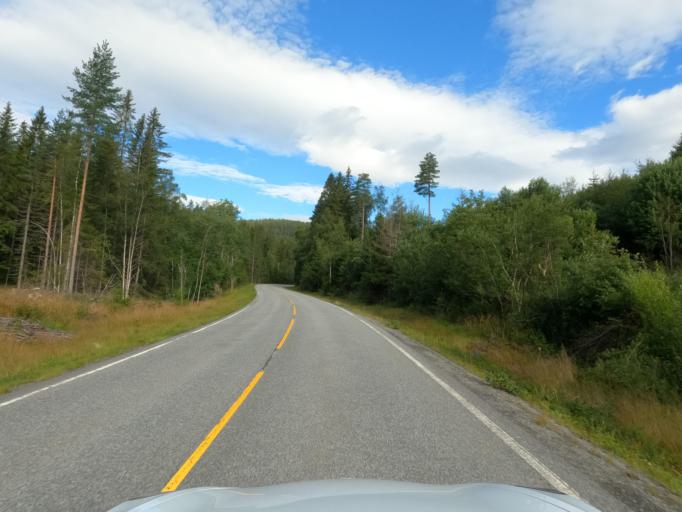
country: NO
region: Telemark
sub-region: Notodden
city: Notodden
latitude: 59.7347
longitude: 9.3283
